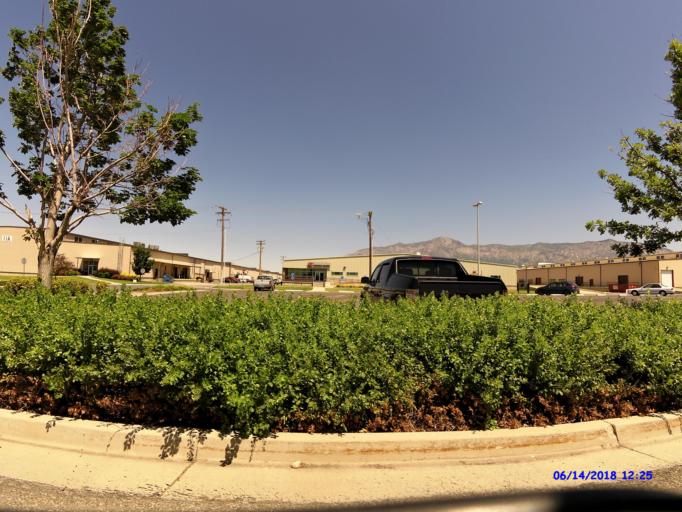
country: US
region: Utah
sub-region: Weber County
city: Harrisville
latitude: 41.2585
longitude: -112.0001
